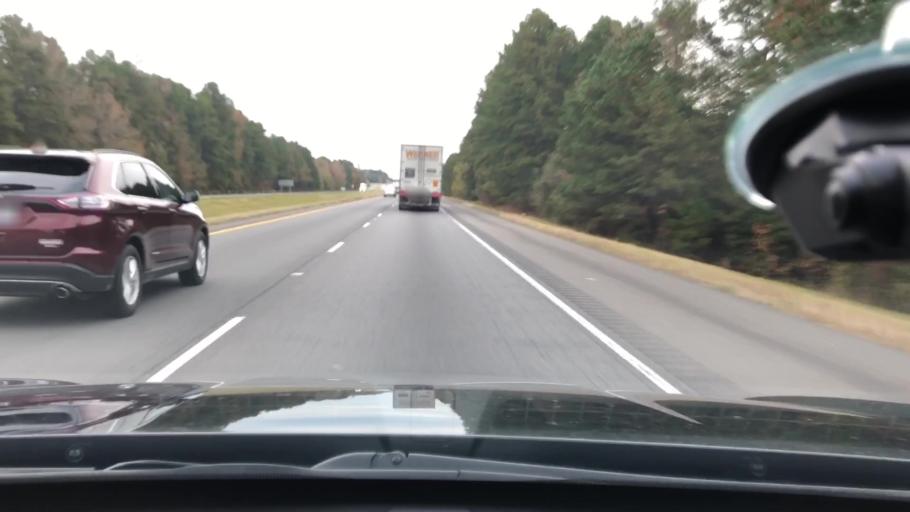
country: US
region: Arkansas
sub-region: Clark County
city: Arkadelphia
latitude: 34.0615
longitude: -93.1273
